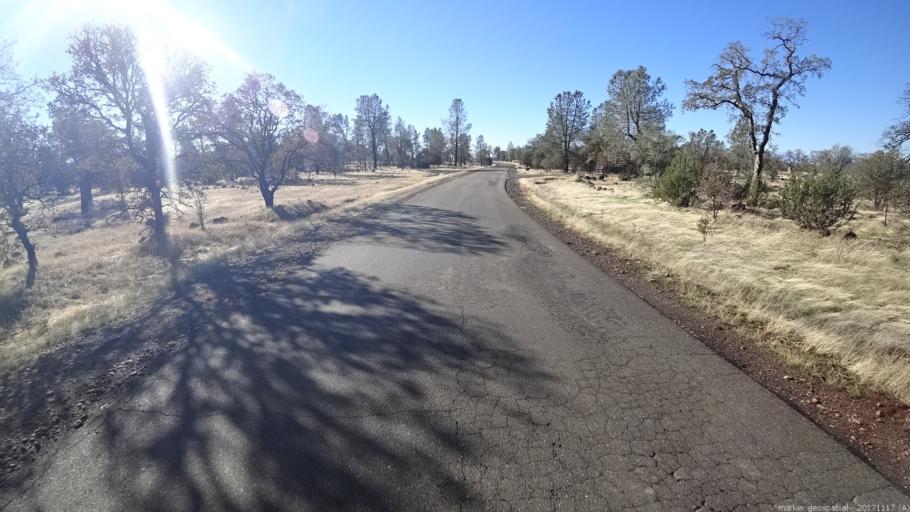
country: US
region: California
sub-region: Shasta County
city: Palo Cedro
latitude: 40.4469
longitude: -122.1150
